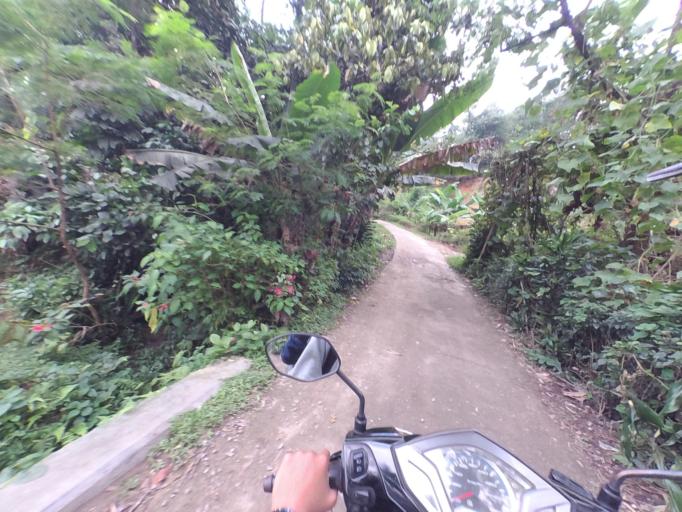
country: ID
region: West Java
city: Ciampea
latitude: -6.6838
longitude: 106.6605
